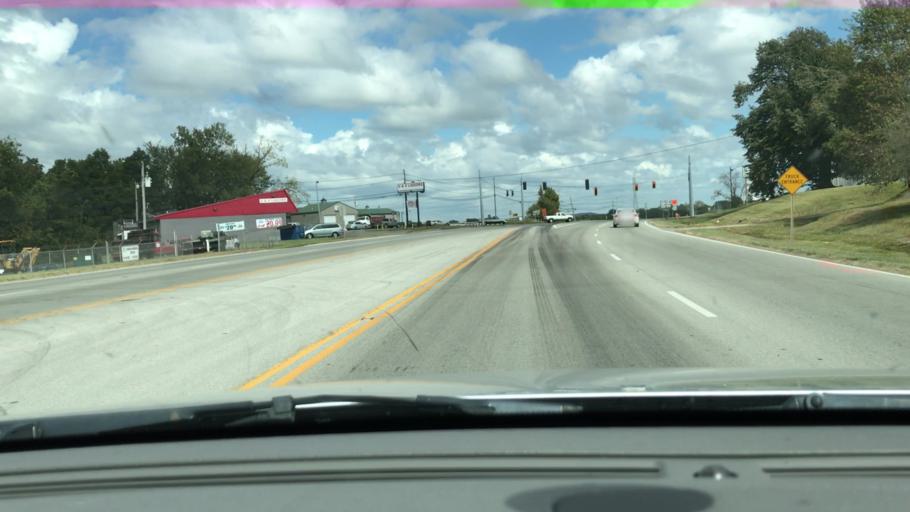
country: US
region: Kentucky
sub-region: Warren County
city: Bowling Green
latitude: 37.0152
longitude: -86.3774
